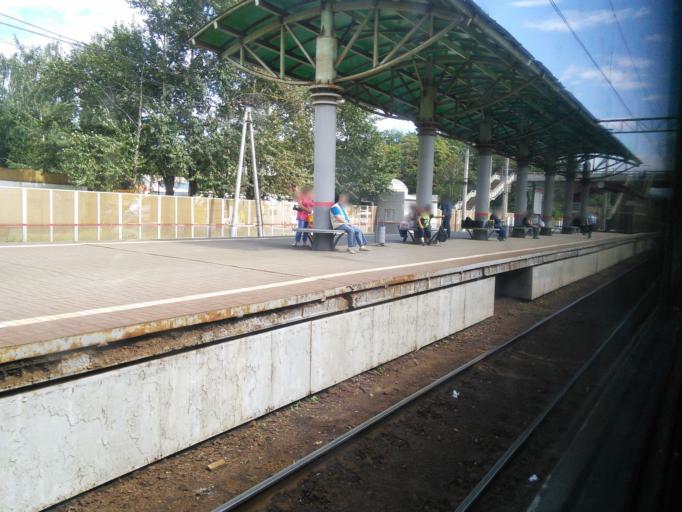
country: RU
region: Moscow
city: Zhulebino
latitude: 55.6987
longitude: 37.8644
